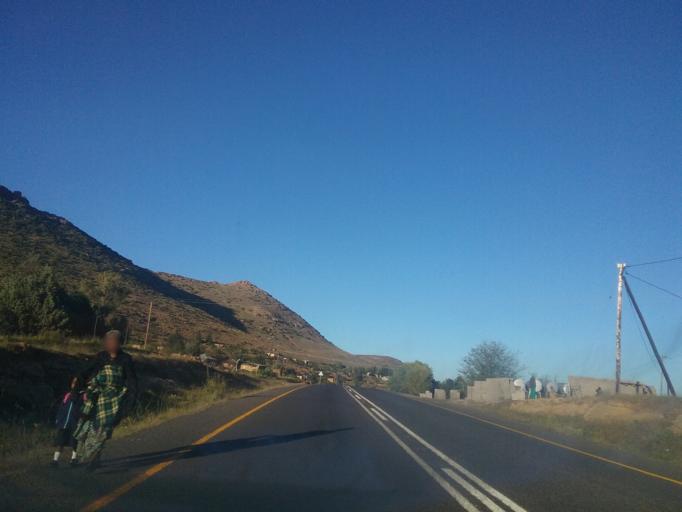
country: LS
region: Mohale's Hoek District
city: Mohale's Hoek
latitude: -30.1770
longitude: 27.4351
